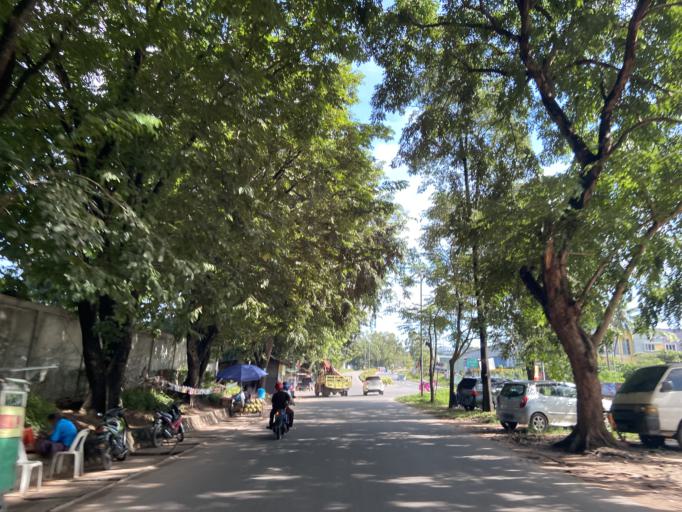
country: SG
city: Singapore
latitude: 1.1689
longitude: 104.0117
